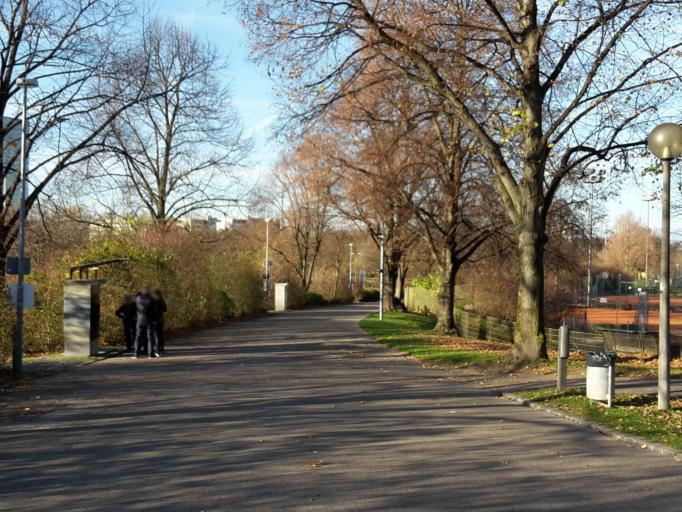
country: DE
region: Bavaria
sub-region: Upper Bavaria
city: Munich
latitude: 48.1710
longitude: 11.5426
